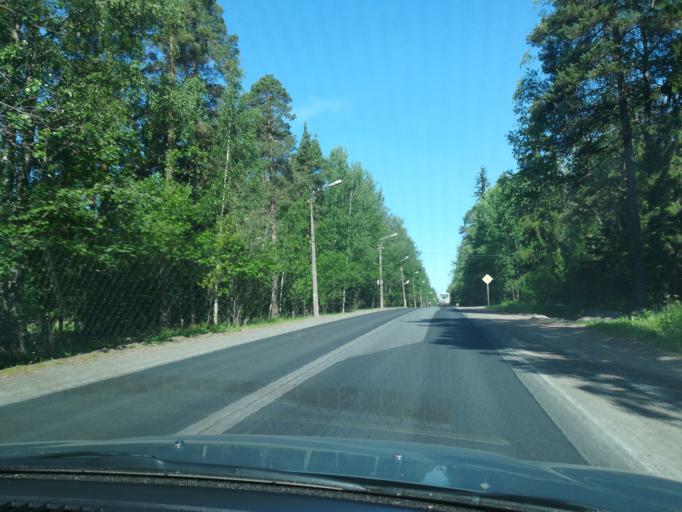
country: RU
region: Leningrad
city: Svetogorsk
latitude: 61.1001
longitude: 28.8732
